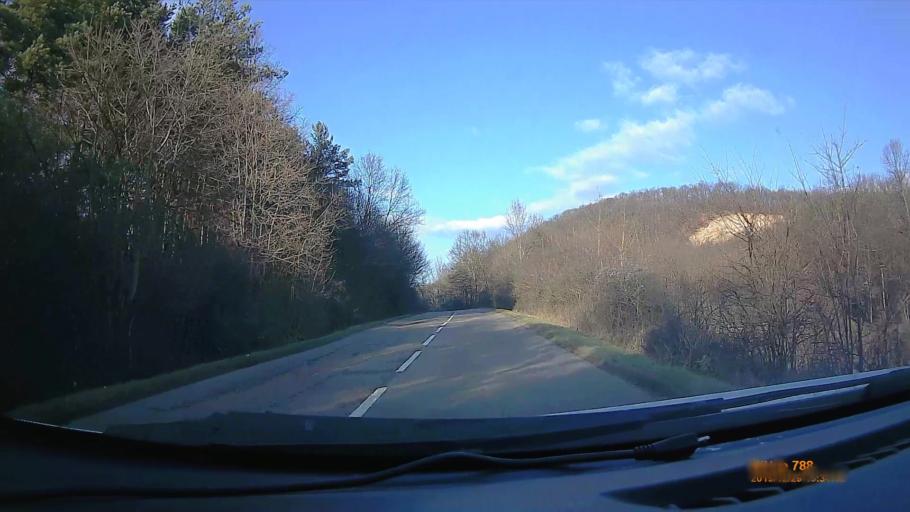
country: HU
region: Heves
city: Sirok
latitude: 47.9043
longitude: 20.1794
